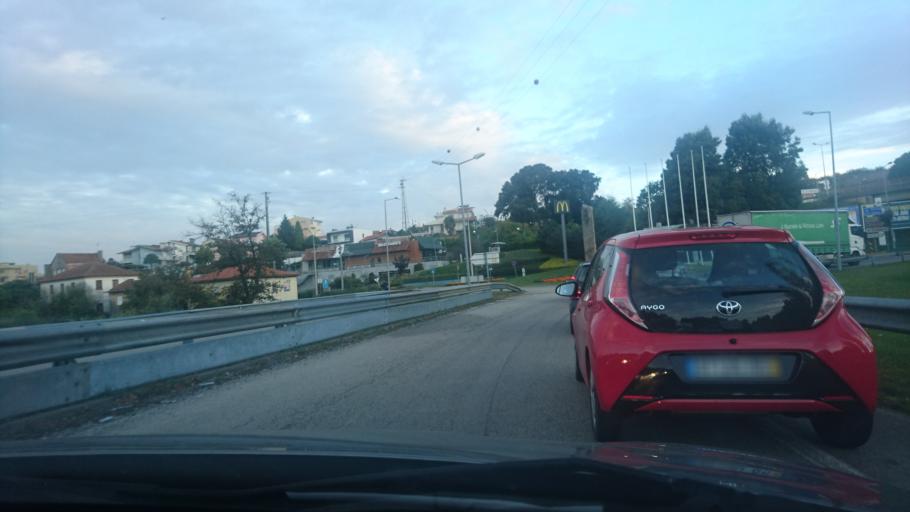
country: PT
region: Aveiro
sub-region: Sao Joao da Madeira
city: Sao Joao da Madeira
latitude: 40.8932
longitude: -8.4798
